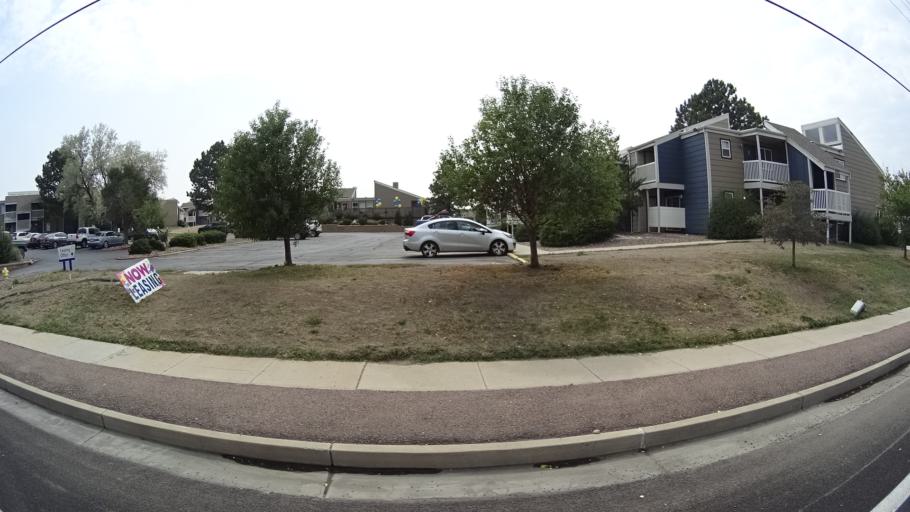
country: US
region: Colorado
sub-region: El Paso County
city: Stratmoor
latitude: 38.8253
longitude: -104.7511
